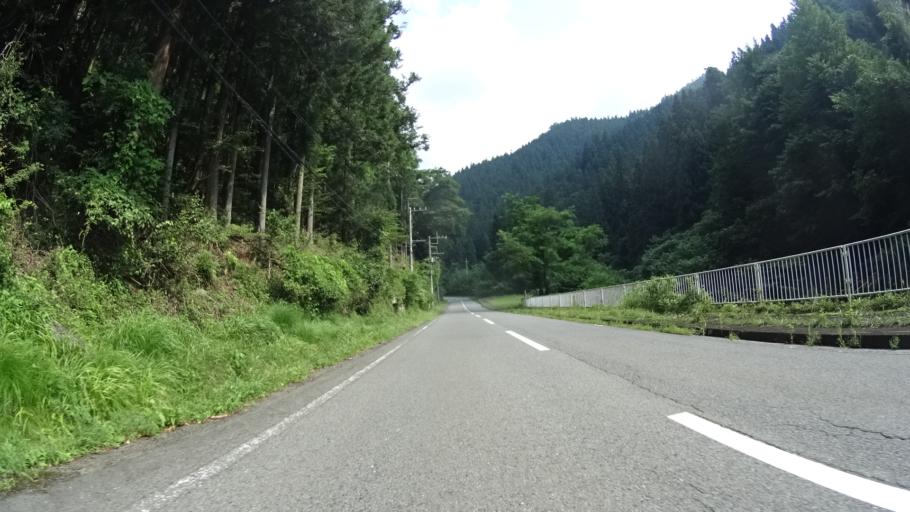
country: JP
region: Gunma
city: Tomioka
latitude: 36.0784
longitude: 138.8250
